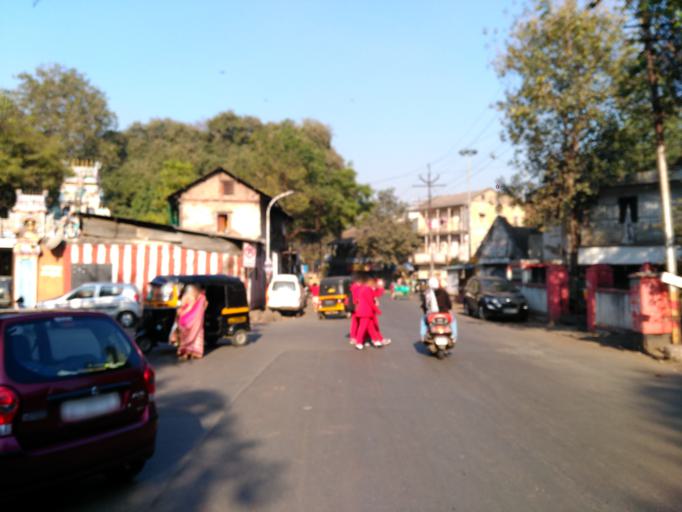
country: IN
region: Maharashtra
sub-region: Pune Division
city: Pune
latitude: 18.5162
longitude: 73.8744
